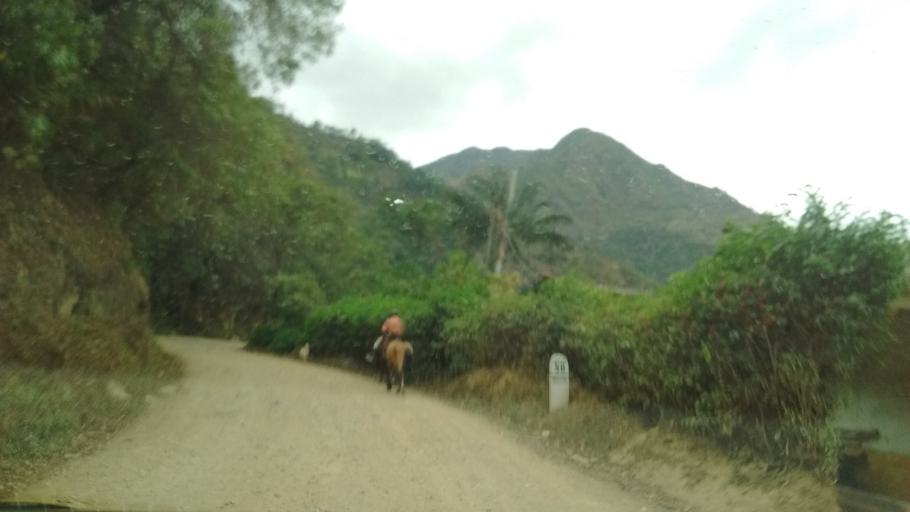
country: CO
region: Cauca
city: La Vega
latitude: 2.0428
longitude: -76.7993
